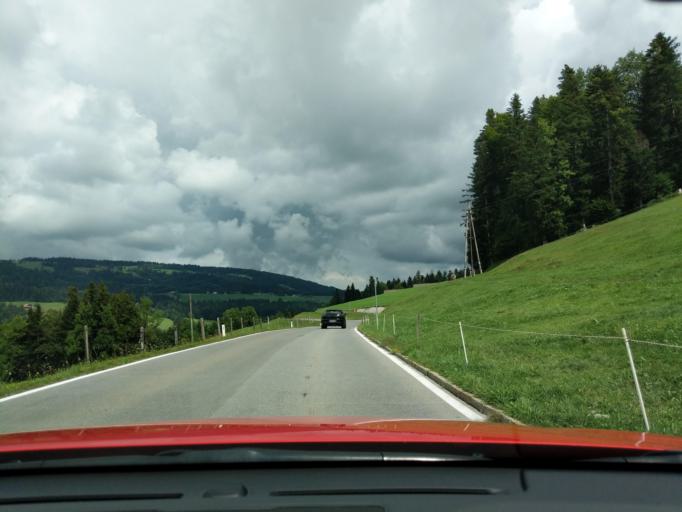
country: AT
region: Vorarlberg
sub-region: Politischer Bezirk Bregenz
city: Riefensberg
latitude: 47.5011
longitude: 9.9460
